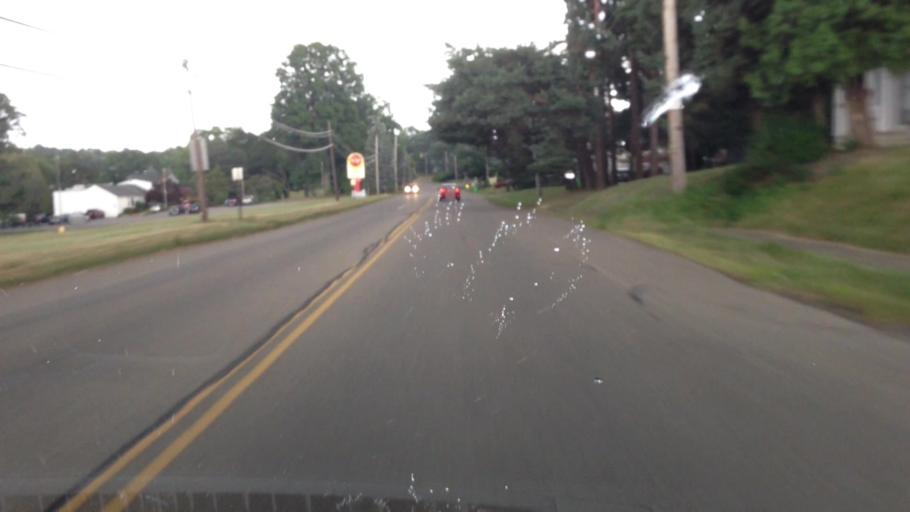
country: US
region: Ohio
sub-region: Summit County
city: Barberton
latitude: 41.0204
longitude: -81.5815
